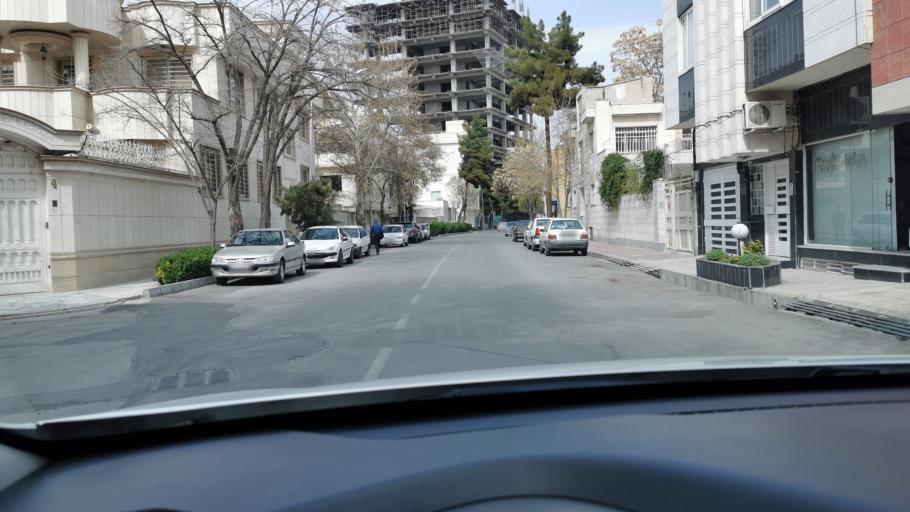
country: IR
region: Razavi Khorasan
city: Mashhad
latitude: 36.2938
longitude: 59.5749
